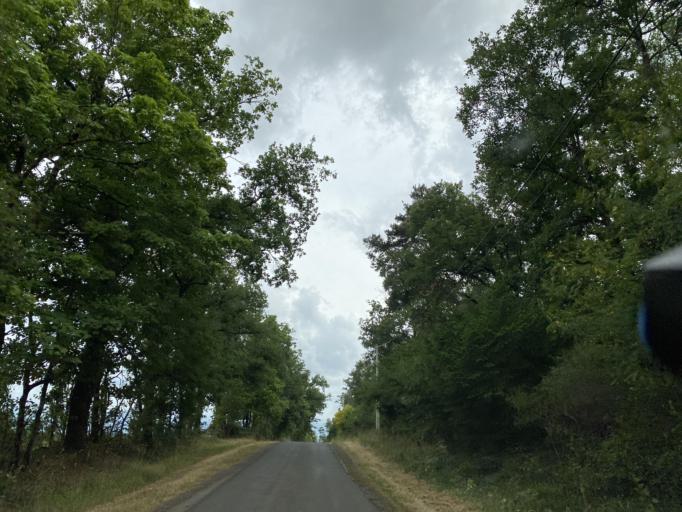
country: FR
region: Auvergne
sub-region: Departement du Puy-de-Dome
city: Peschadoires
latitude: 45.7527
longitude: 3.4557
